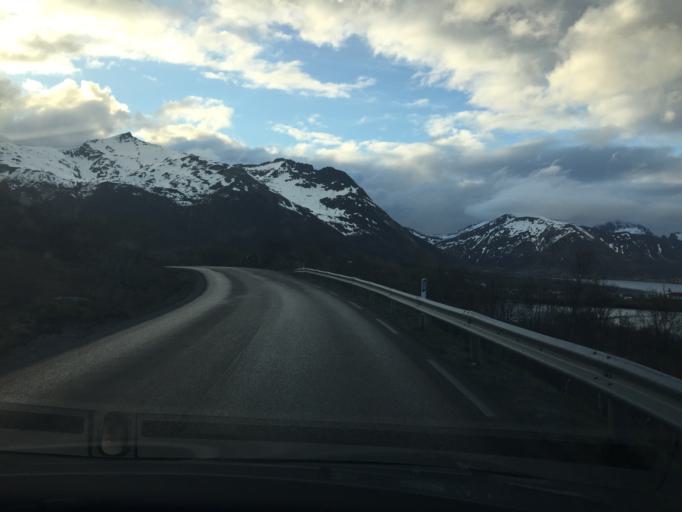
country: NO
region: Nordland
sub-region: Vagan
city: Svolvaer
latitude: 68.3159
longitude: 14.7145
